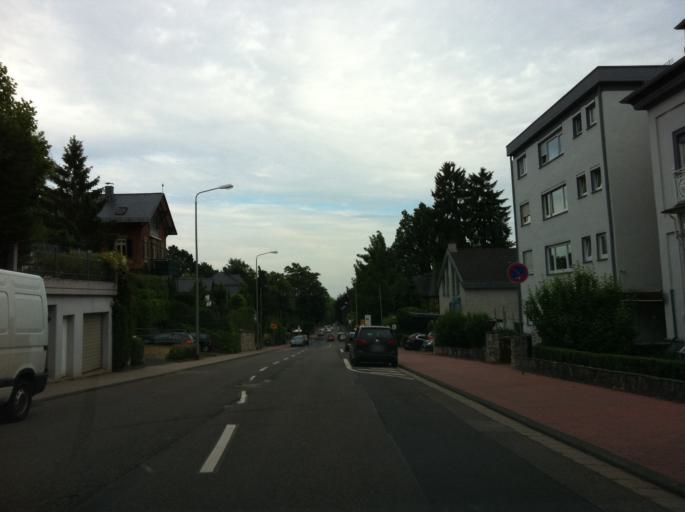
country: DE
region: Hesse
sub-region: Regierungsbezirk Darmstadt
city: Bad Soden am Taunus
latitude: 50.1513
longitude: 8.4946
